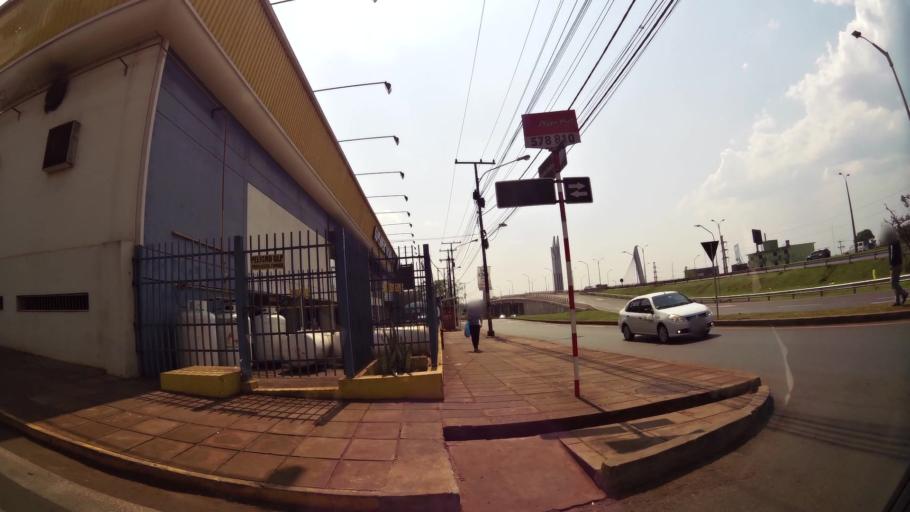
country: PY
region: Alto Parana
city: Ciudad del Este
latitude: -25.5080
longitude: -54.6371
